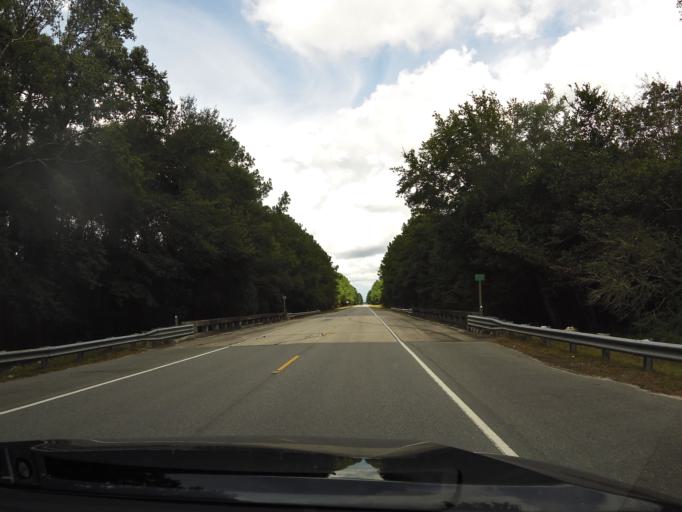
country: US
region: Georgia
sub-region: Brantley County
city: Nahunta
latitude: 31.0571
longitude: -82.0157
